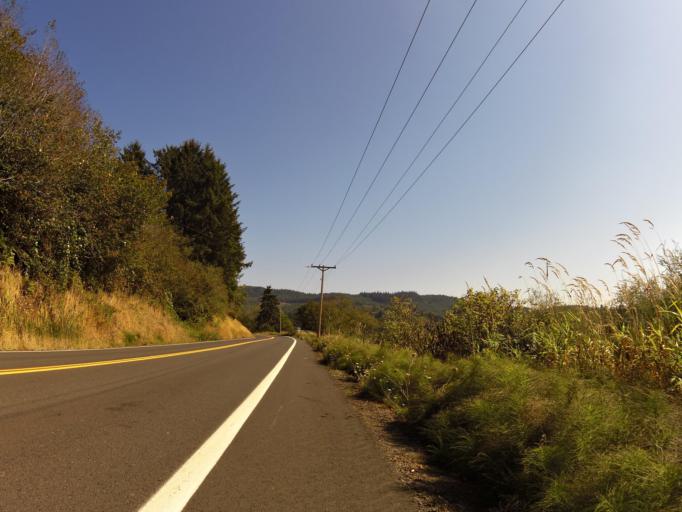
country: US
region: Oregon
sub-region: Tillamook County
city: Pacific City
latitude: 45.1800
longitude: -123.9343
